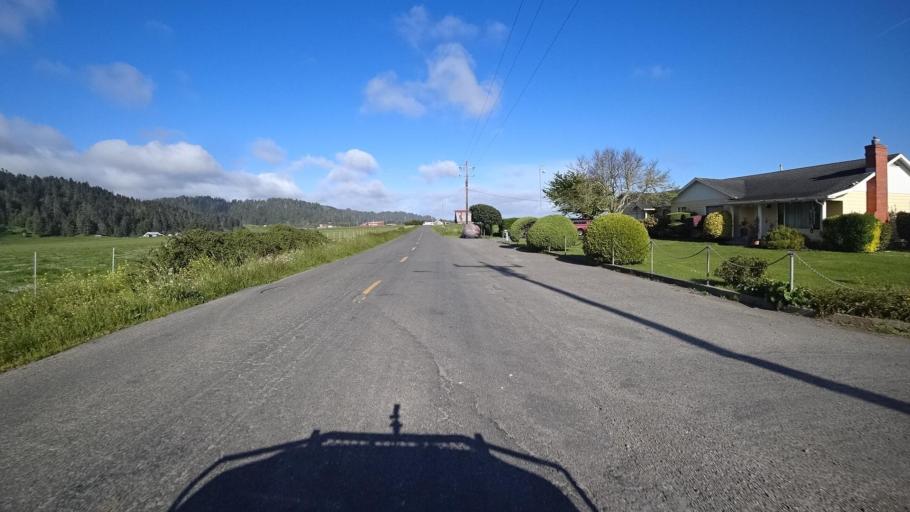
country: US
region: California
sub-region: Humboldt County
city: Ferndale
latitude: 40.5726
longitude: -124.2320
